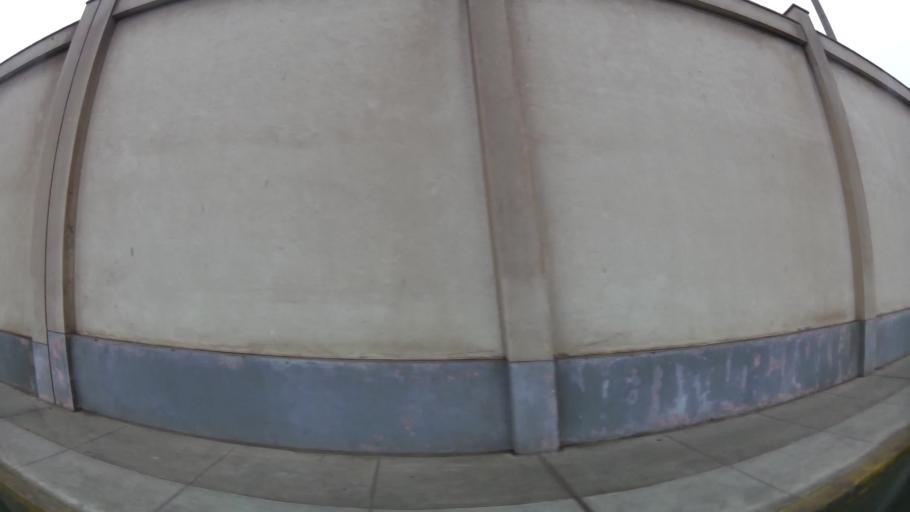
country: PE
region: Callao
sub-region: Callao
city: Callao
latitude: -12.0750
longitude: -77.1202
